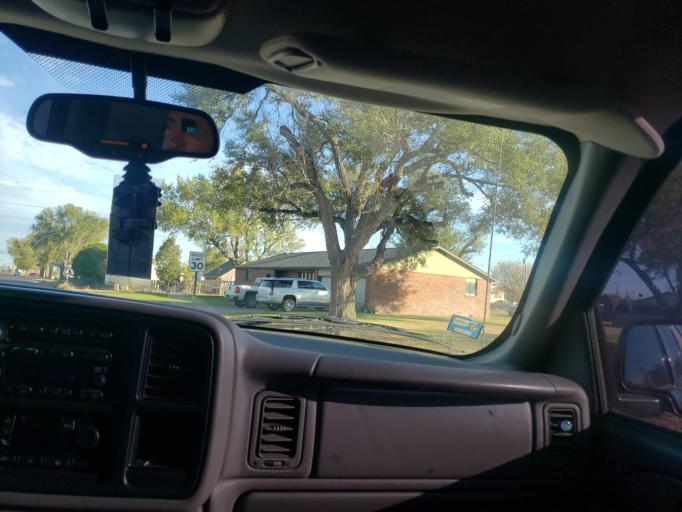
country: US
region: Kansas
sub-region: Finney County
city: Garden City
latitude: 37.9673
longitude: -100.8833
